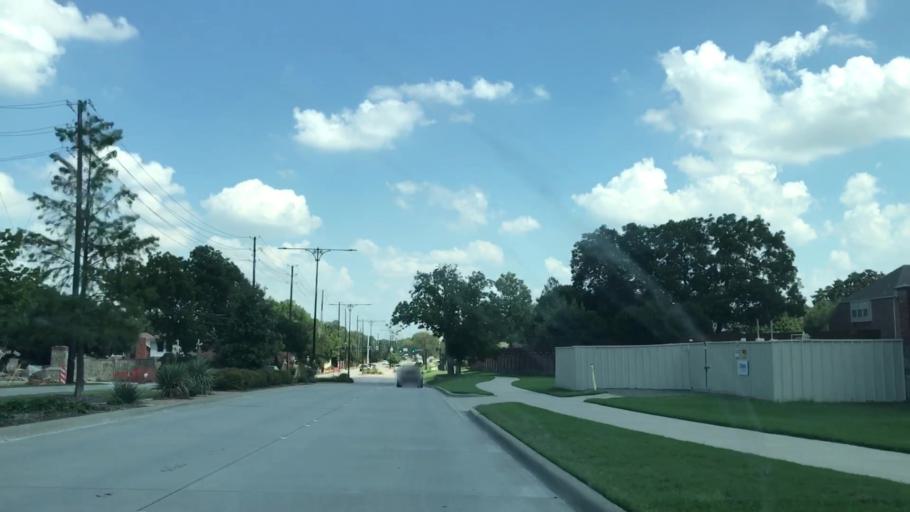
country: US
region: Texas
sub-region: Dallas County
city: Coppell
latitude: 32.9696
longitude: -97.0030
